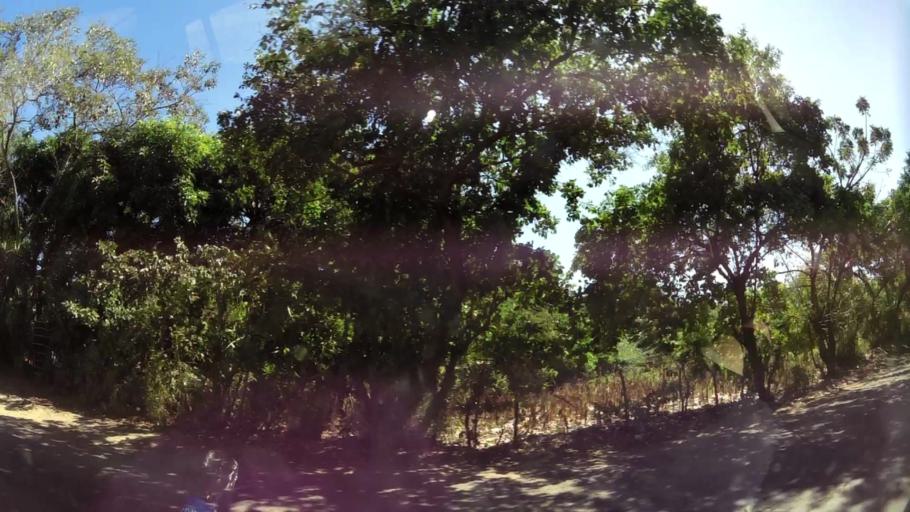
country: SV
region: Ahuachapan
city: Ahuachapan
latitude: 13.9403
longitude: -89.8440
